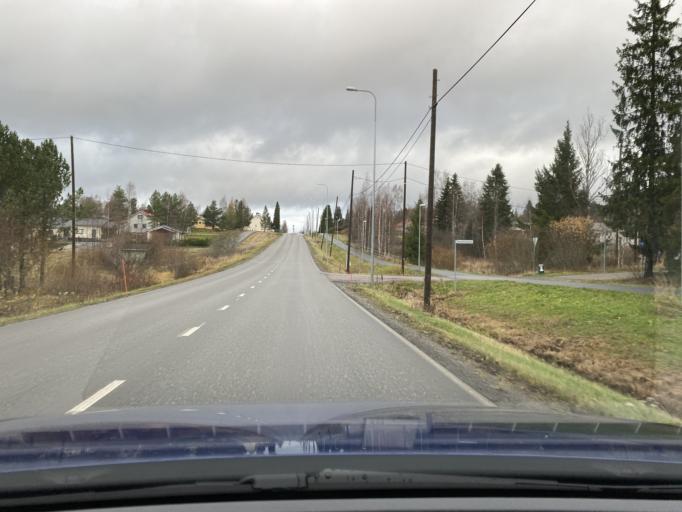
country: FI
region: Pirkanmaa
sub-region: Tampere
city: Lempaeaelae
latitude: 61.3701
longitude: 23.7785
